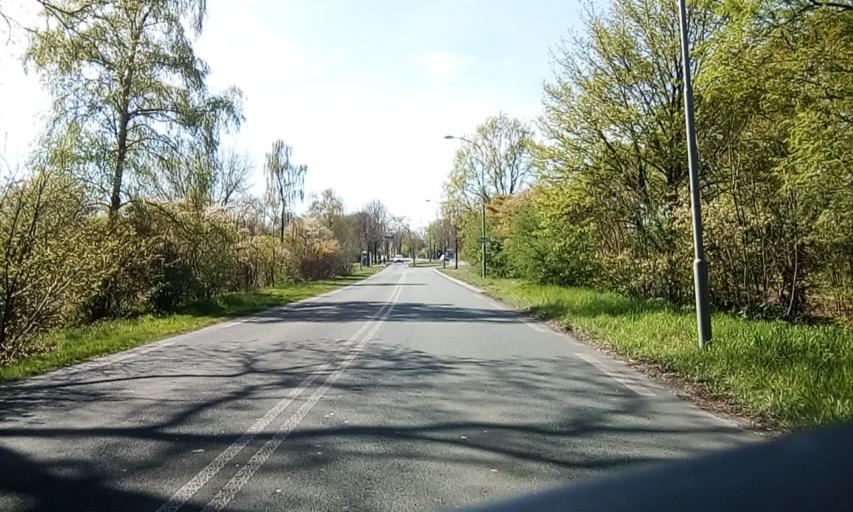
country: NL
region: Gelderland
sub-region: Gemeente Wijchen
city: Wijchen
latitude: 51.8186
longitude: 5.7324
